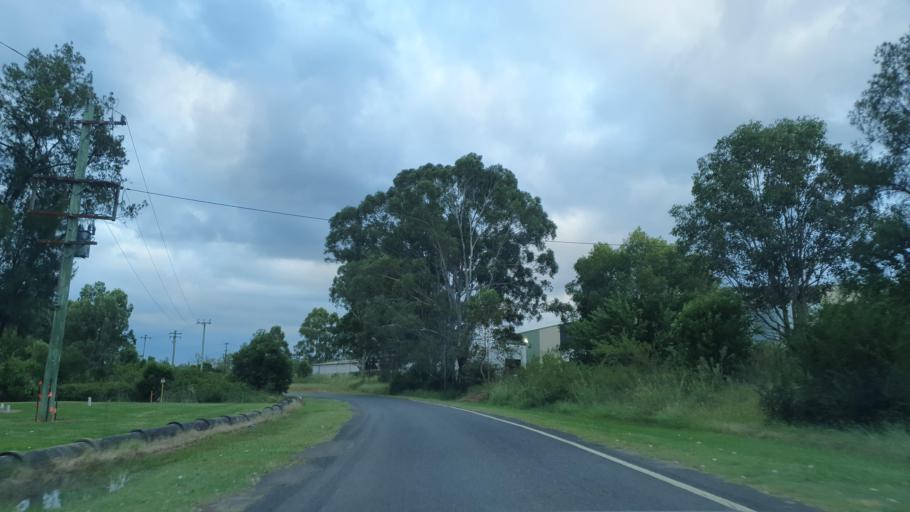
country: AU
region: New South Wales
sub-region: Penrith Municipality
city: Werrington County
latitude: -33.7422
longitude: 150.7631
